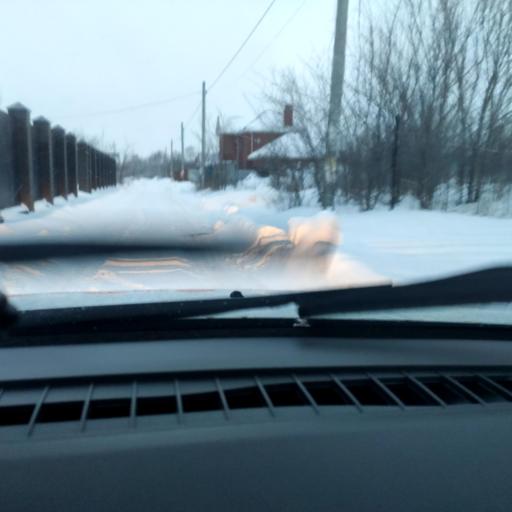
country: RU
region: Samara
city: Dubovyy Umet
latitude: 53.0288
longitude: 50.2301
